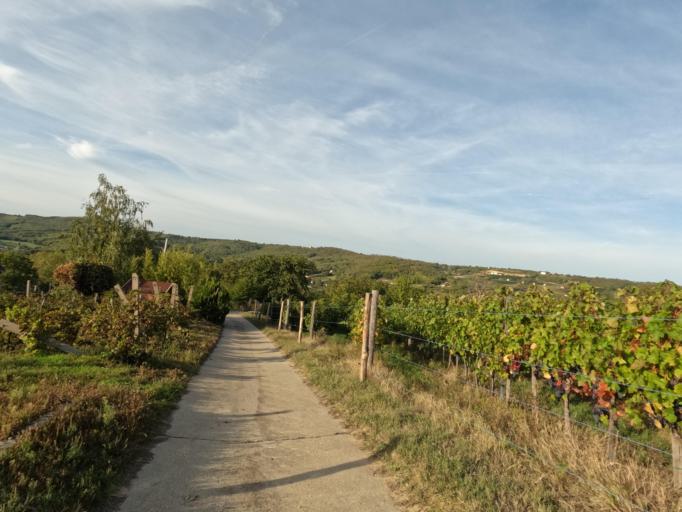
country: HU
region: Tolna
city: Szekszard
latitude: 46.3296
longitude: 18.6715
